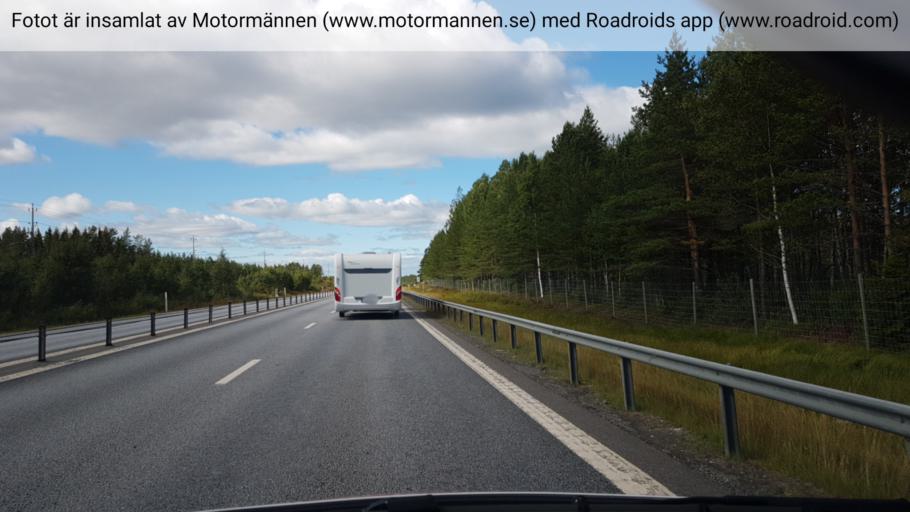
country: SE
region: Vaesterbotten
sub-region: Nordmalings Kommun
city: Nordmaling
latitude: 63.5842
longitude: 19.5905
